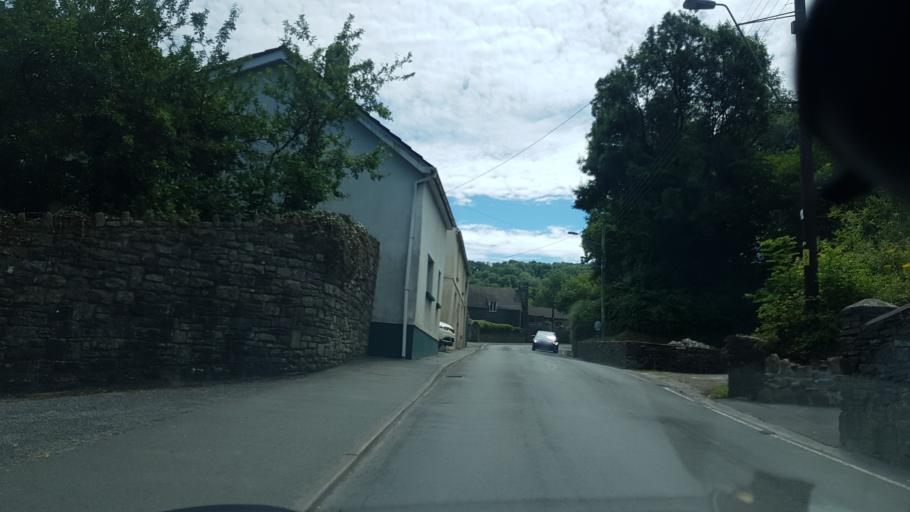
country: GB
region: Wales
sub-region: Carmarthenshire
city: Saint Clears
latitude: 51.7673
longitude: -4.4634
